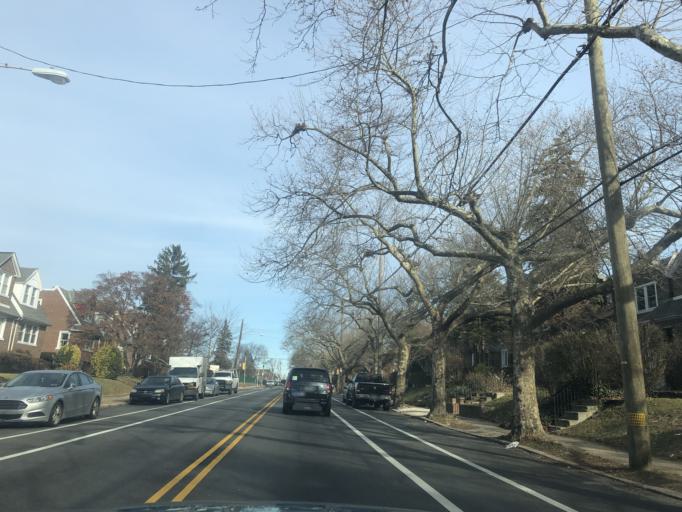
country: US
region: Pennsylvania
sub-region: Montgomery County
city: Wyndmoor
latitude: 40.0622
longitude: -75.1629
